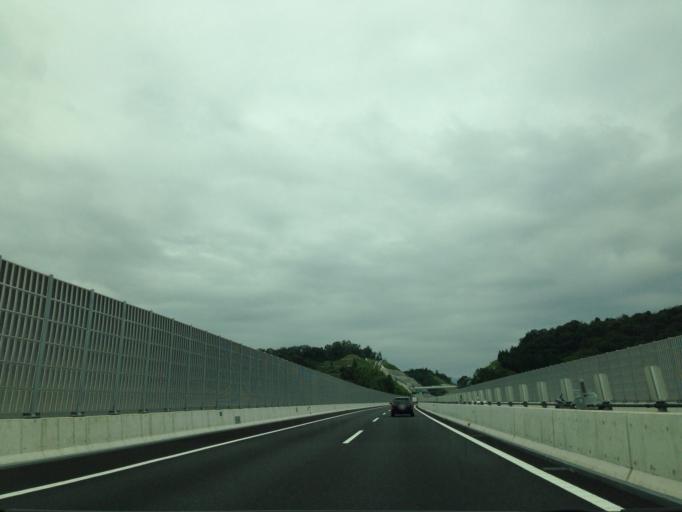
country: JP
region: Aichi
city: Okazaki
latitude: 35.0083
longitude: 137.2284
